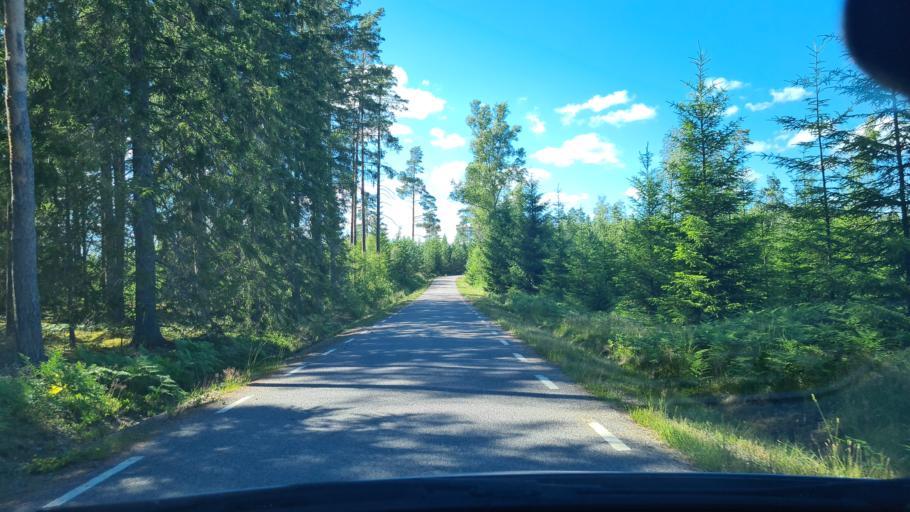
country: SE
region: OEstergoetland
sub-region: Norrkopings Kommun
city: Krokek
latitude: 58.7048
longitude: 16.4291
